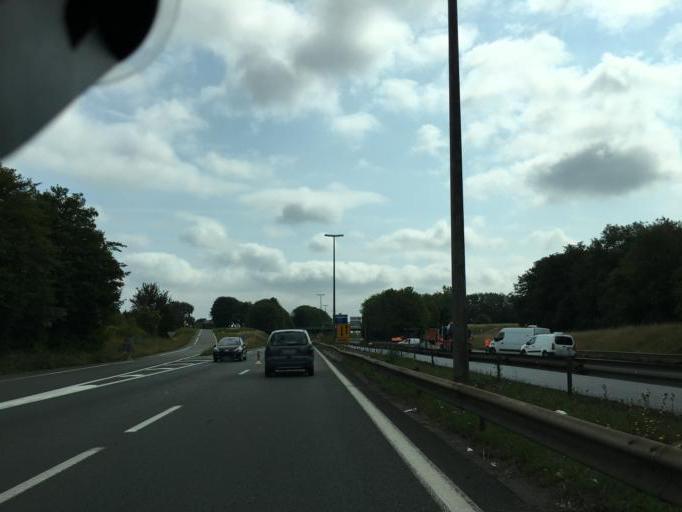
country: FR
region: Nord-Pas-de-Calais
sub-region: Departement du Pas-de-Calais
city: Loison-sous-Lens
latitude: 50.4454
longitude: 2.8410
